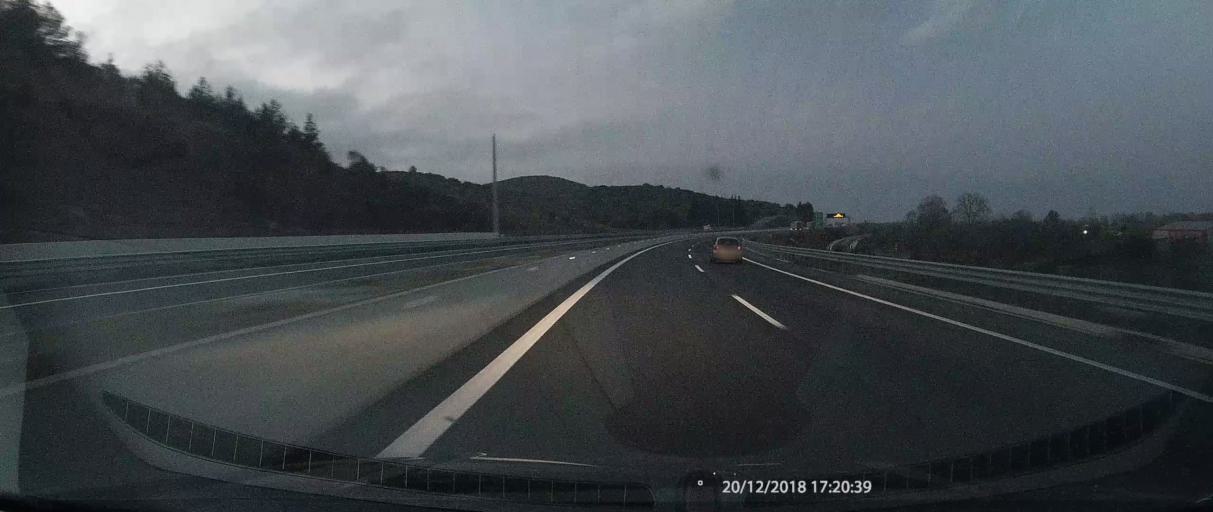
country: GR
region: Thessaly
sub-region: Nomos Larisis
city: Pyrgetos
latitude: 39.9684
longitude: 22.6412
